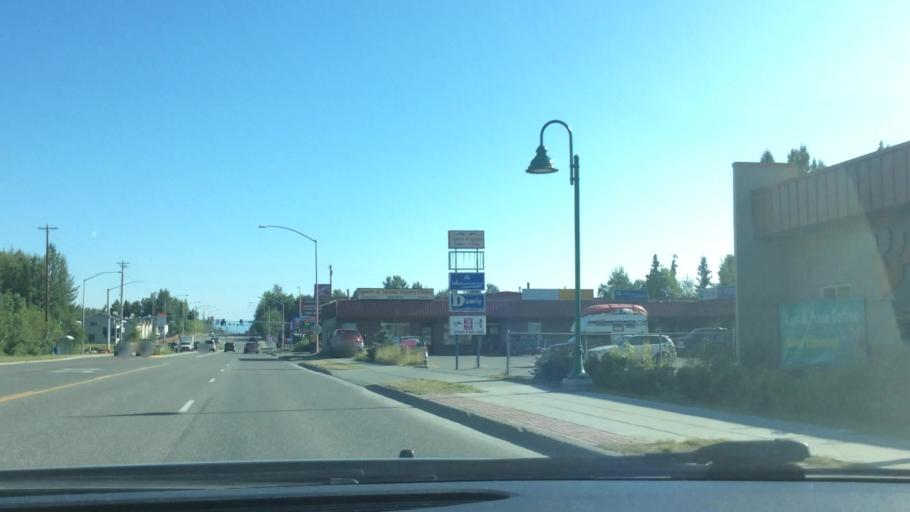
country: US
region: Alaska
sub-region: Anchorage Municipality
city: Anchorage
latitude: 61.1608
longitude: -149.8344
